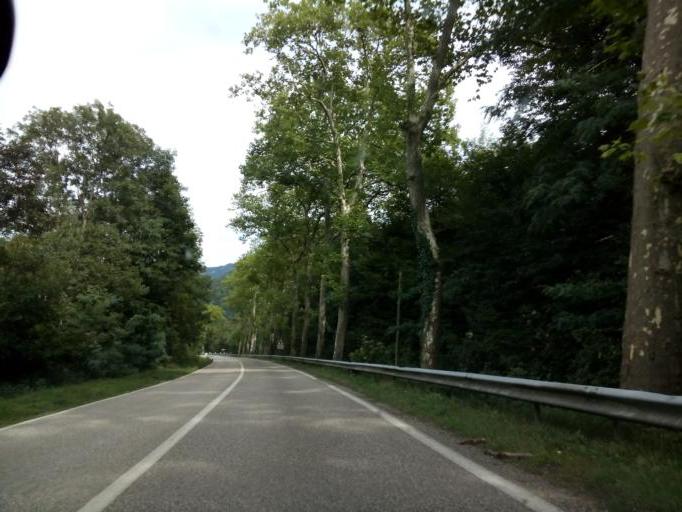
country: FR
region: Rhone-Alpes
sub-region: Departement de l'Isere
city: Notre-Dame-de-Mesage
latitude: 45.0499
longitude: 5.7855
